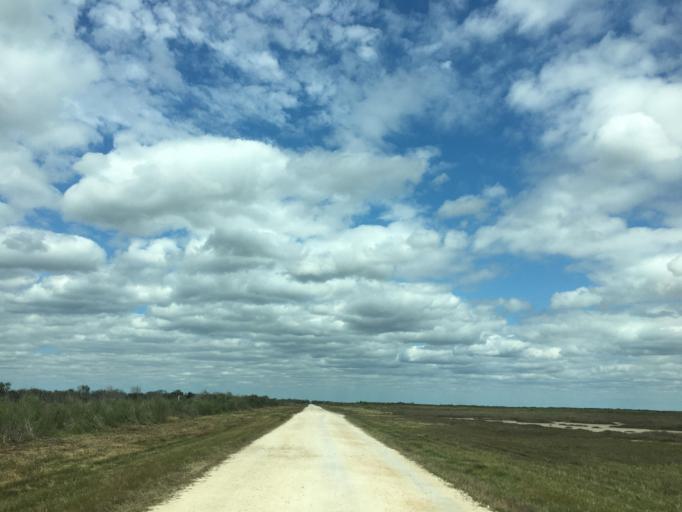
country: US
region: Texas
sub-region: Brazoria County
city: Oyster Creek
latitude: 29.0426
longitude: -95.2681
